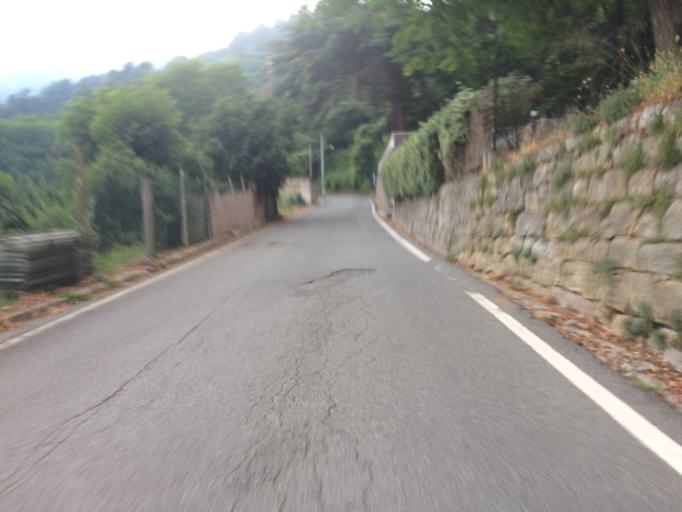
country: IT
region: Liguria
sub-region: Provincia di Imperia
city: Seborga
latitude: 43.8531
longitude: 7.7243
